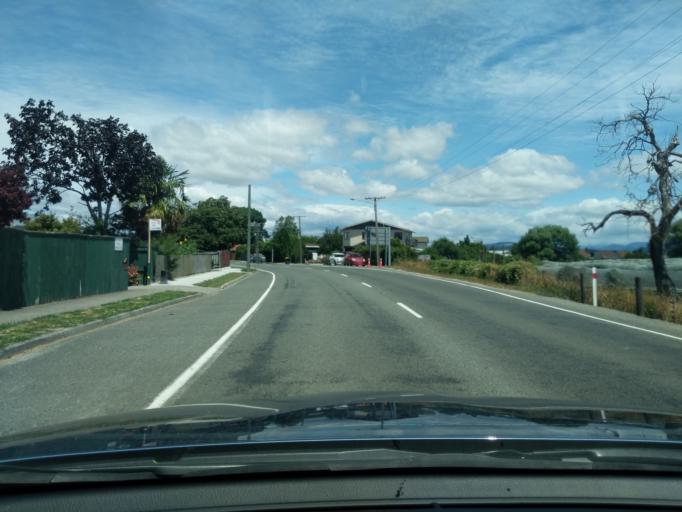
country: NZ
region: Tasman
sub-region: Tasman District
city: Motueka
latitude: -41.1025
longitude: 173.0118
